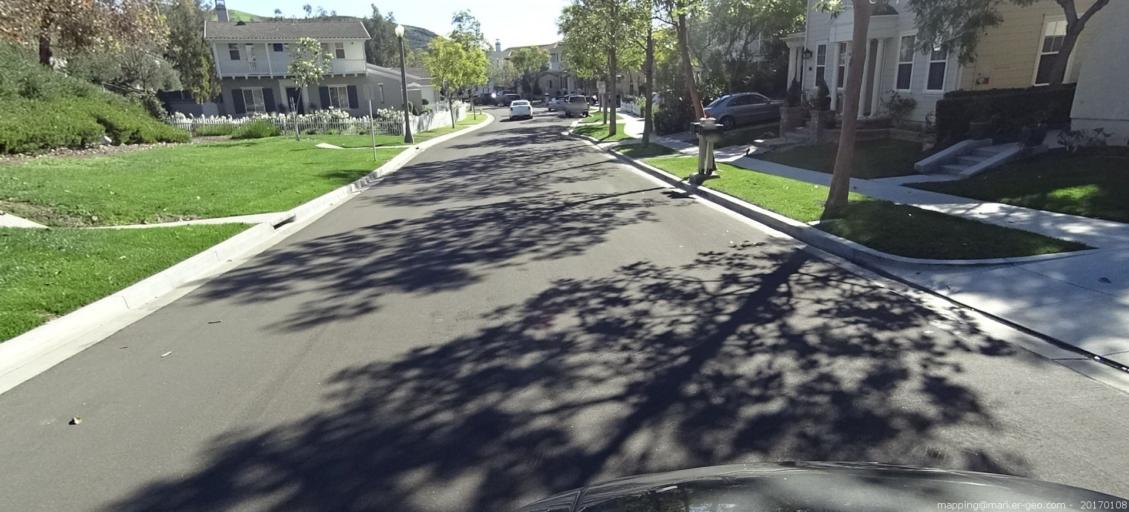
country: US
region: California
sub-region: Orange County
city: Ladera Ranch
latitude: 33.5710
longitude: -117.6330
